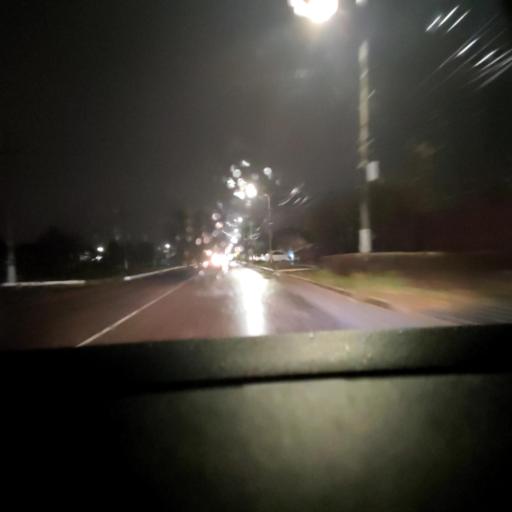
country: RU
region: Voronezj
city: Semiluki
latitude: 51.6930
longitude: 39.0336
